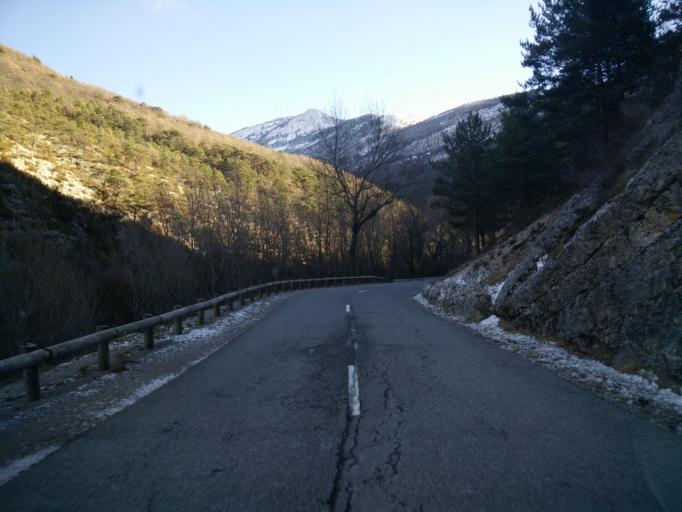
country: FR
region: Provence-Alpes-Cote d'Azur
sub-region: Departement des Alpes-de-Haute-Provence
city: Castellane
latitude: 43.8203
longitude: 6.4328
